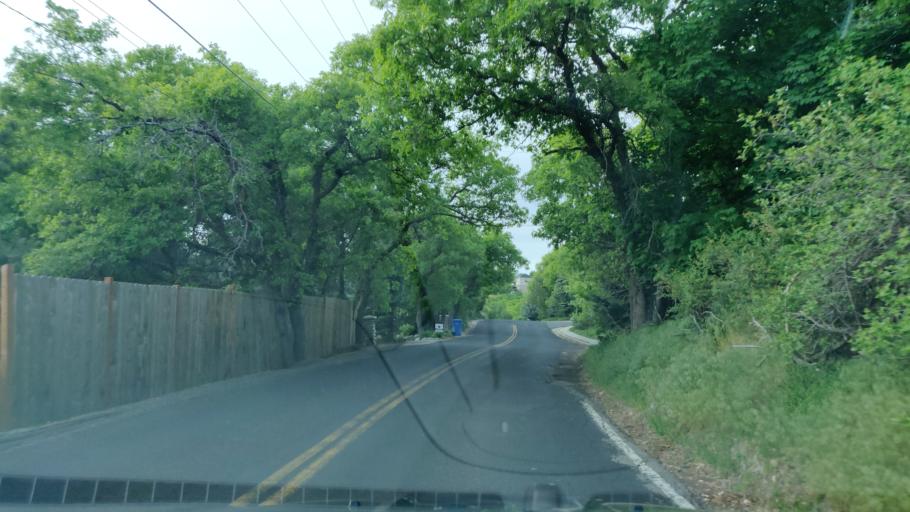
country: US
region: Utah
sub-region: Salt Lake County
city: Granite
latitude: 40.5945
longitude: -111.8008
